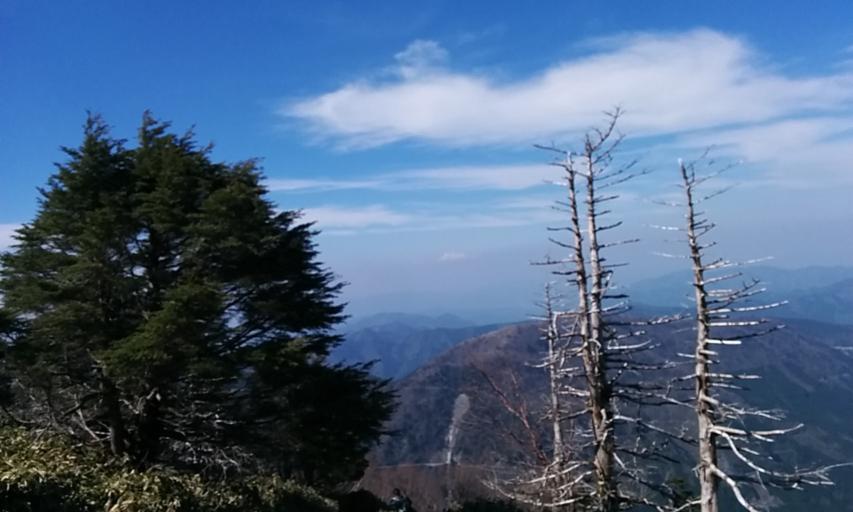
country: JP
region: Tokushima
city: Wakimachi
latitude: 33.8558
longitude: 134.0958
